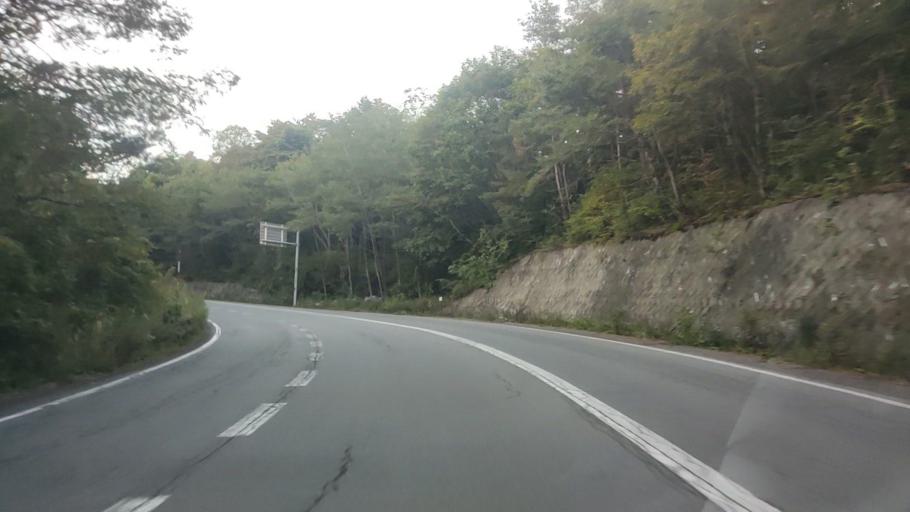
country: JP
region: Nagano
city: Komoro
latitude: 36.3907
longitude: 138.5837
